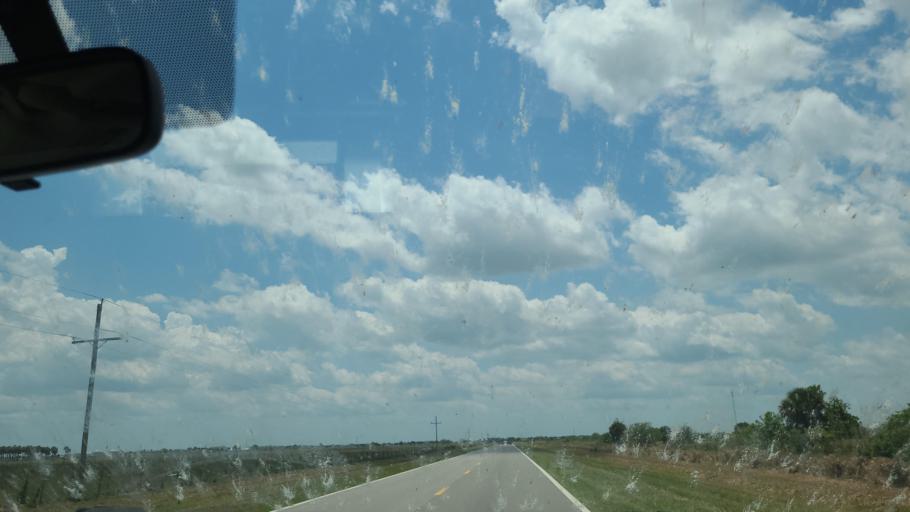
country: US
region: Florida
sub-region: Glades County
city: Buckhead Ridge
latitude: 27.2492
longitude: -81.0539
